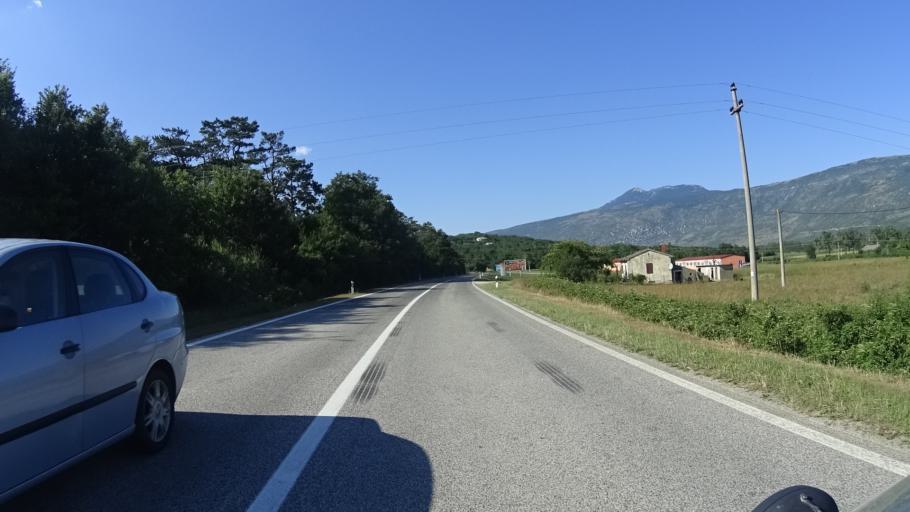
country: HR
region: Istarska
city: Vinez
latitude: 45.2003
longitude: 14.1339
